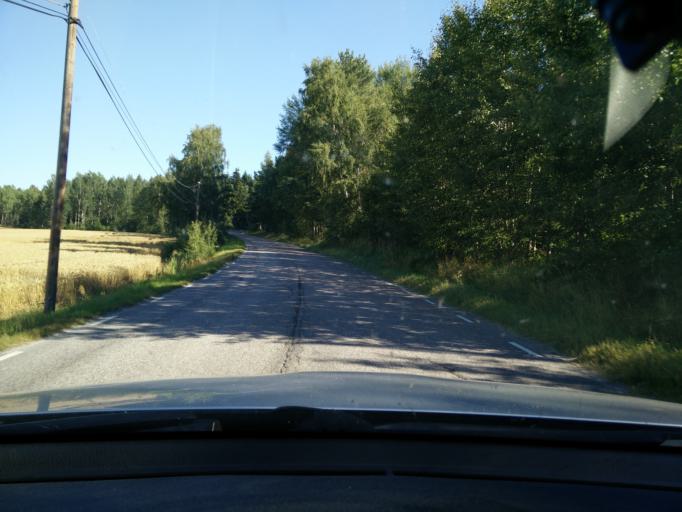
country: SE
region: Stockholm
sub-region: Taby Kommun
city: Taby
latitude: 59.4660
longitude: 18.1627
